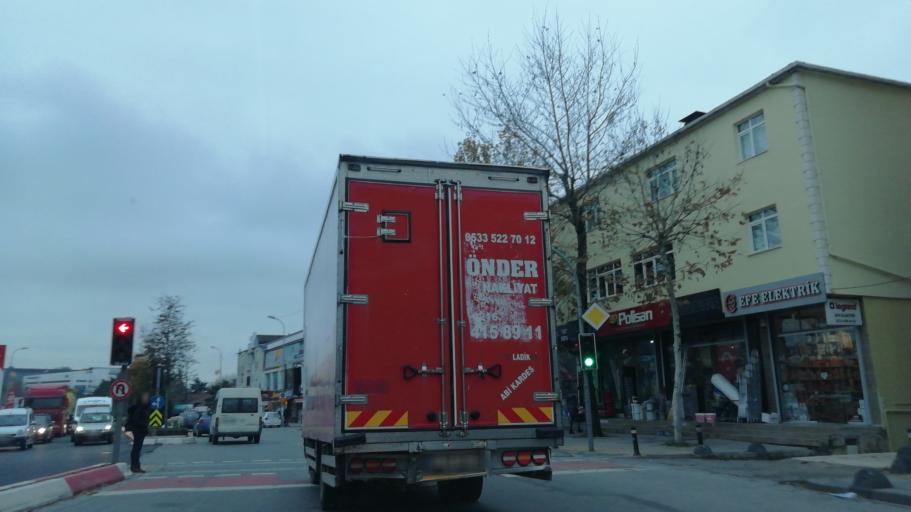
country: TR
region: Istanbul
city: Sultanbeyli
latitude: 40.9715
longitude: 29.2493
